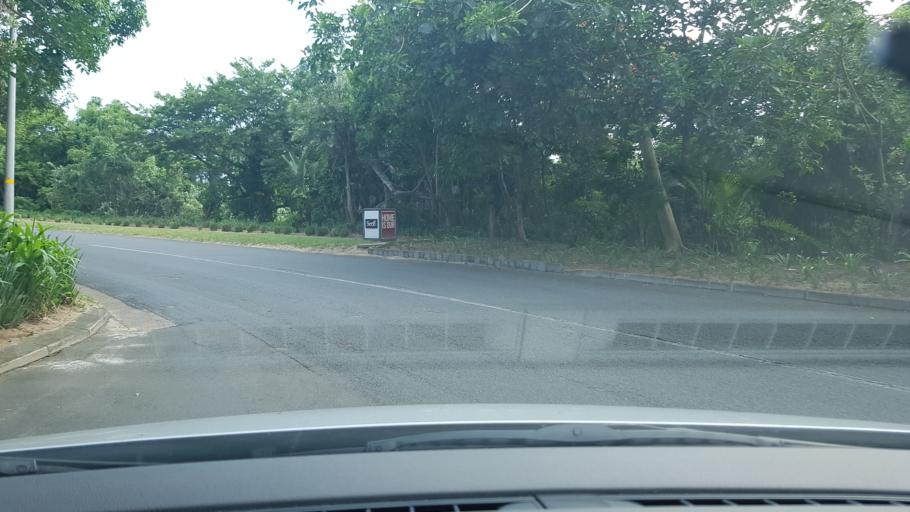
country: ZA
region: KwaZulu-Natal
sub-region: uThungulu District Municipality
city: Richards Bay
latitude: -28.7764
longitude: 32.0997
